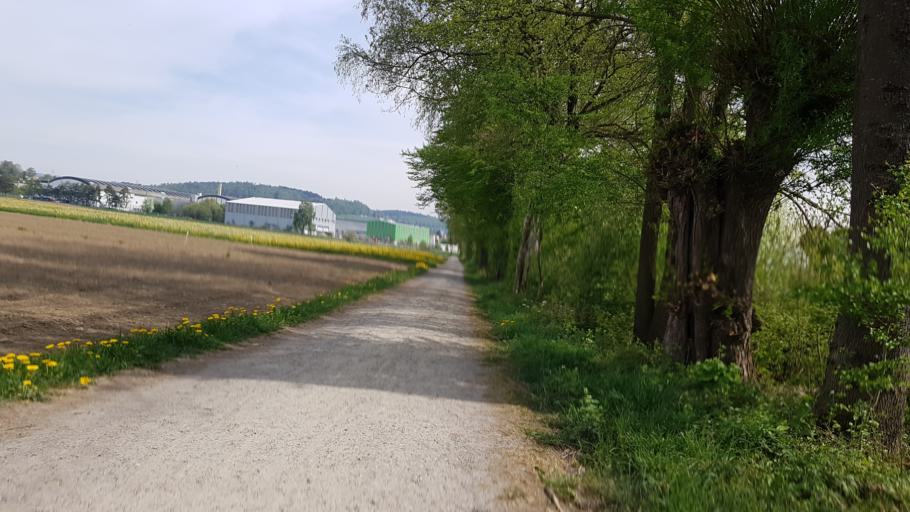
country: CH
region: Aargau
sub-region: Bezirk Kulm
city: Gontenschwil
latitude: 47.2692
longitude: 8.1648
